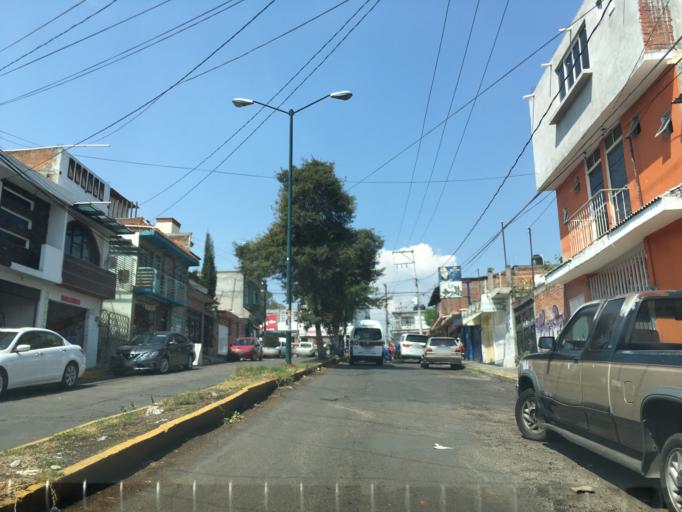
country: MX
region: Michoacan
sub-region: Morelia
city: Montana Monarca (Punta Altozano)
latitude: 19.6684
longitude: -101.1983
